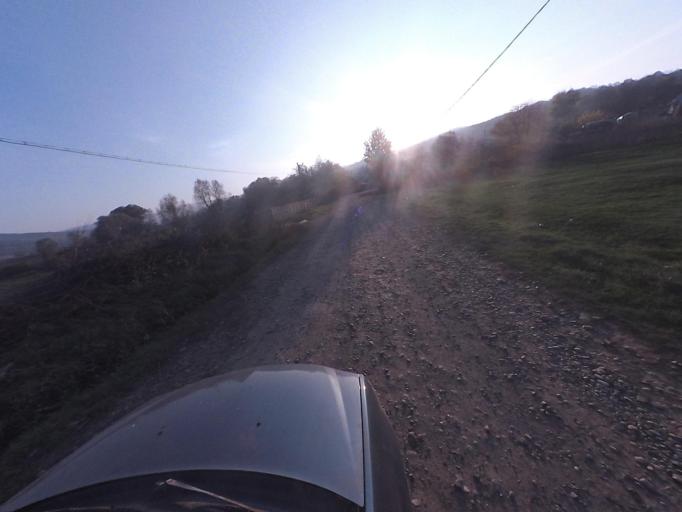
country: RO
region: Vaslui
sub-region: Comuna Bacesti
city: Bacesti
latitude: 46.8088
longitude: 27.2276
